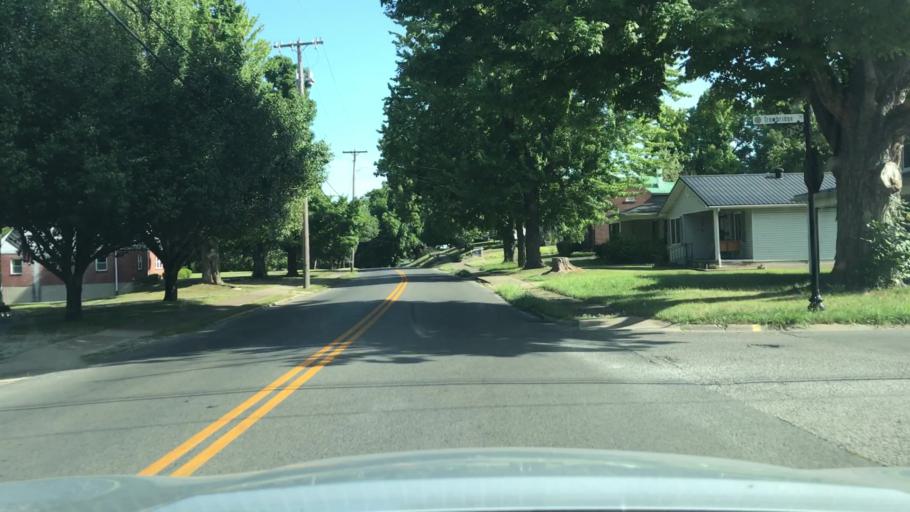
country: US
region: Kentucky
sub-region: Muhlenberg County
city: Greenville
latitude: 37.2053
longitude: -87.1790
